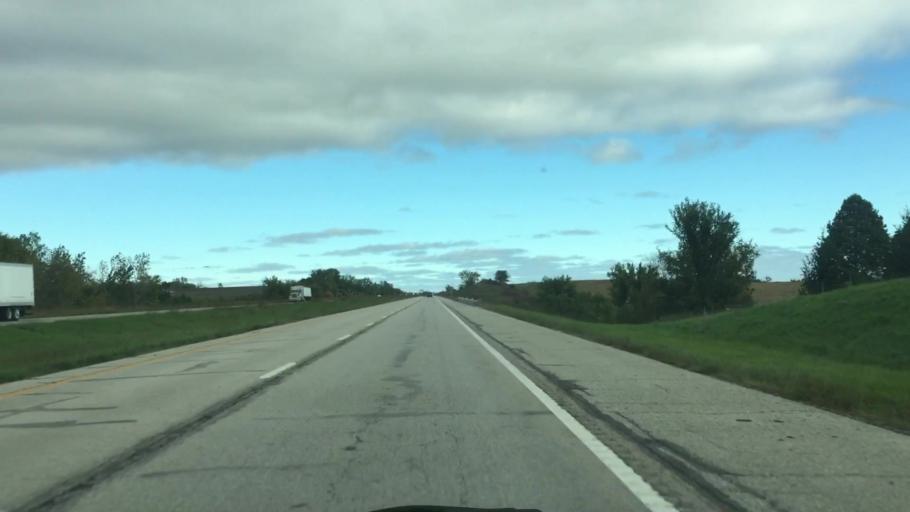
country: US
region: Missouri
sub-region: Harrison County
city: Bethany
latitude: 40.3236
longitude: -94.0114
